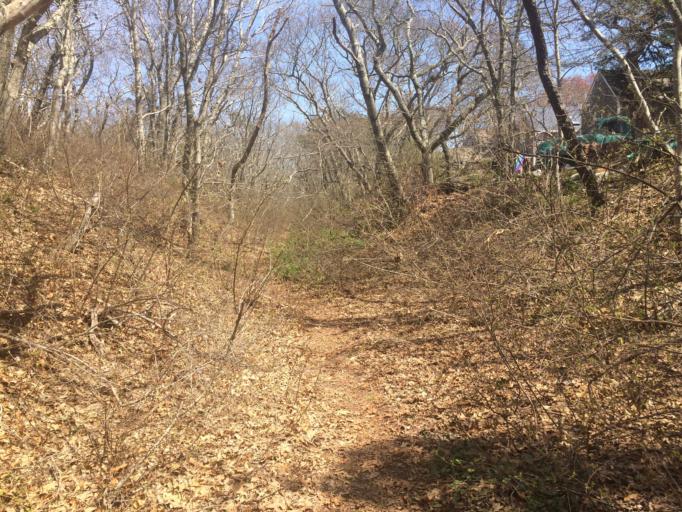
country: US
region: Massachusetts
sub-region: Barnstable County
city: Provincetown
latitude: 42.0646
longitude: -70.1541
